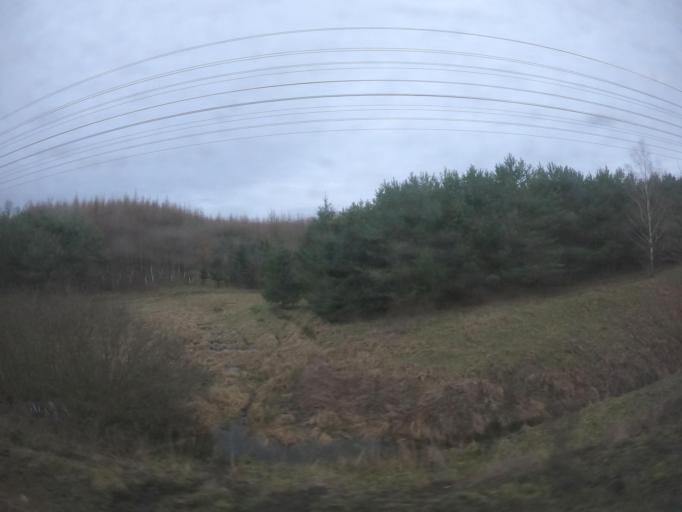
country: PL
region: West Pomeranian Voivodeship
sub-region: Powiat szczecinecki
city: Borne Sulinowo
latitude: 53.6582
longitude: 16.5665
